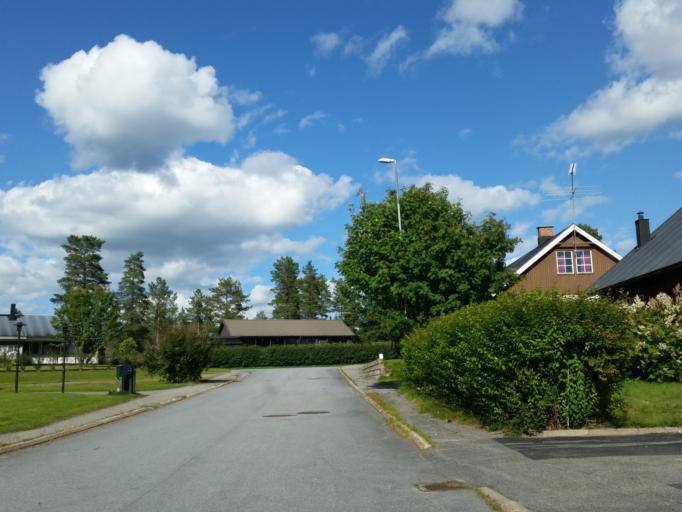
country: SE
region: Vaesterbotten
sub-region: Robertsfors Kommun
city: Robertsfors
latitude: 64.1984
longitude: 20.8438
